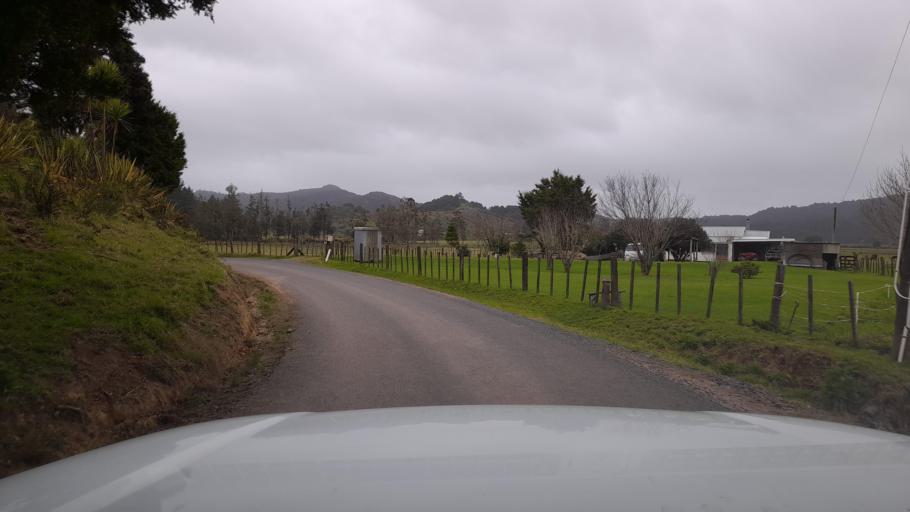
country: NZ
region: Northland
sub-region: Far North District
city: Paihia
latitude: -35.3391
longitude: 174.2343
